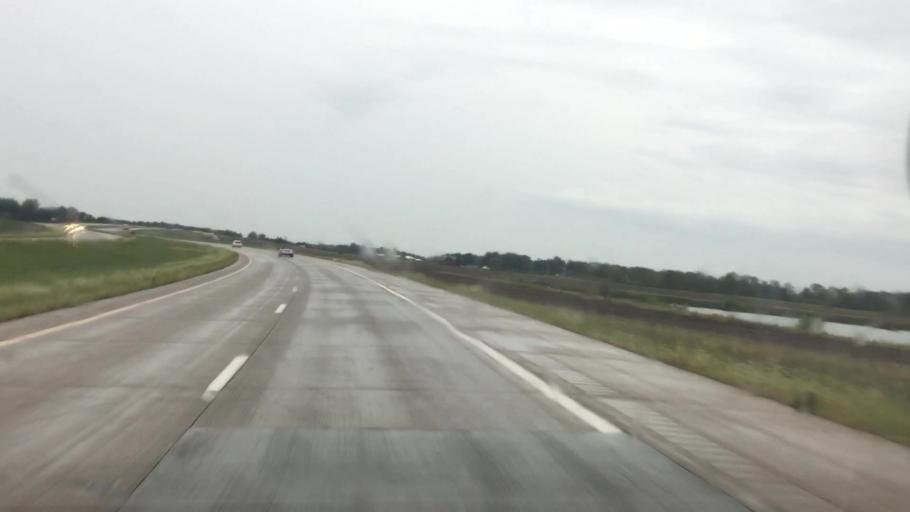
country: US
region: Ohio
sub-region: Defiance County
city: Defiance
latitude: 41.2710
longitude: -84.4228
